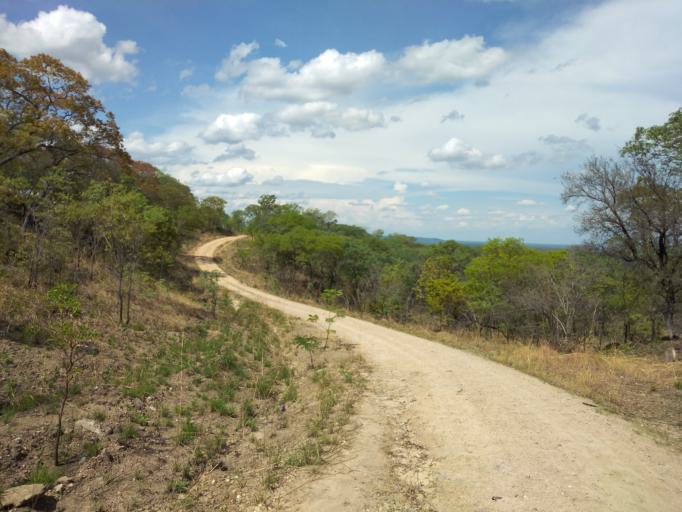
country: ZM
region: Eastern
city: Nyimba
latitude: -14.1202
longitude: 30.1005
